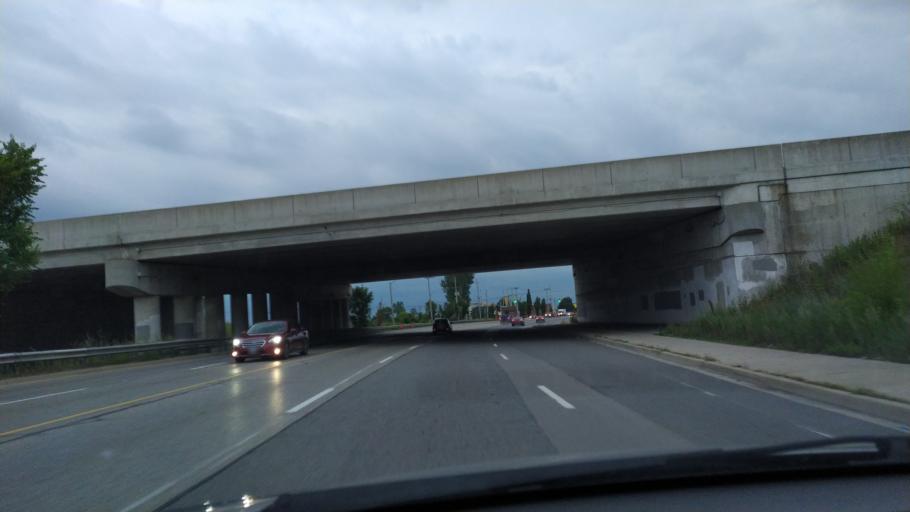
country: CA
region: Ontario
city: Kitchener
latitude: 43.4261
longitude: -80.4333
